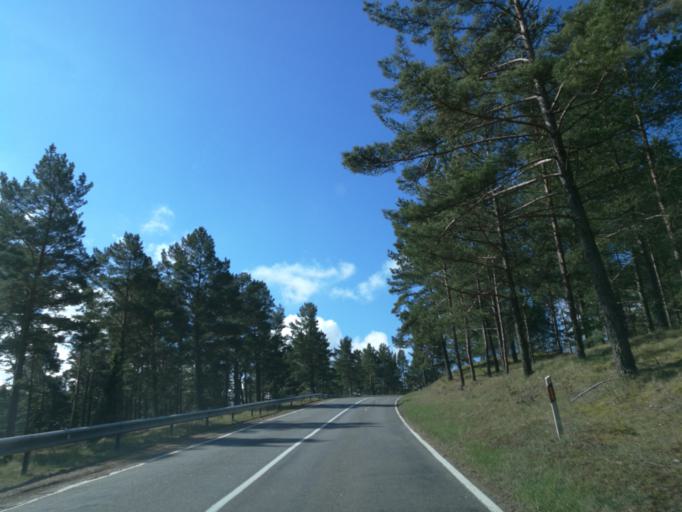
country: LT
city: Neringa
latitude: 55.5147
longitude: 21.1140
